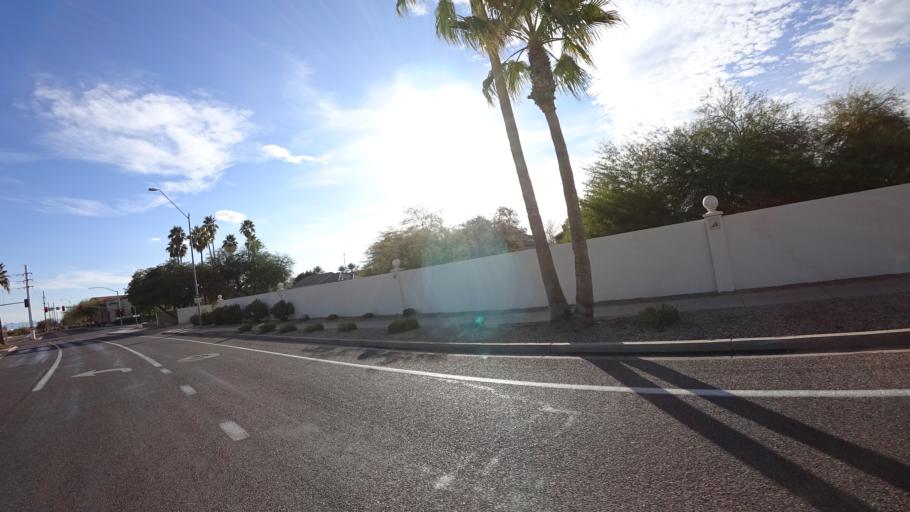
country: US
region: Arizona
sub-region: Maricopa County
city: Sun City
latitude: 33.6106
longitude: -112.2550
